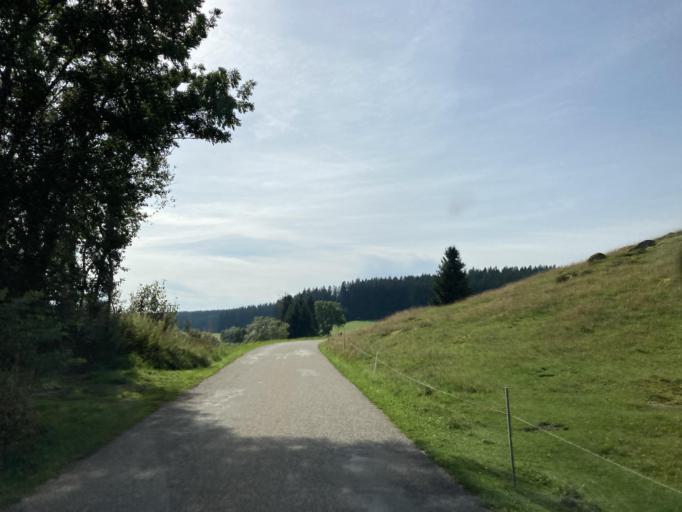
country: DE
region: Baden-Wuerttemberg
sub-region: Freiburg Region
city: Schonwald im Schwarzwald
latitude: 48.0998
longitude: 8.2139
